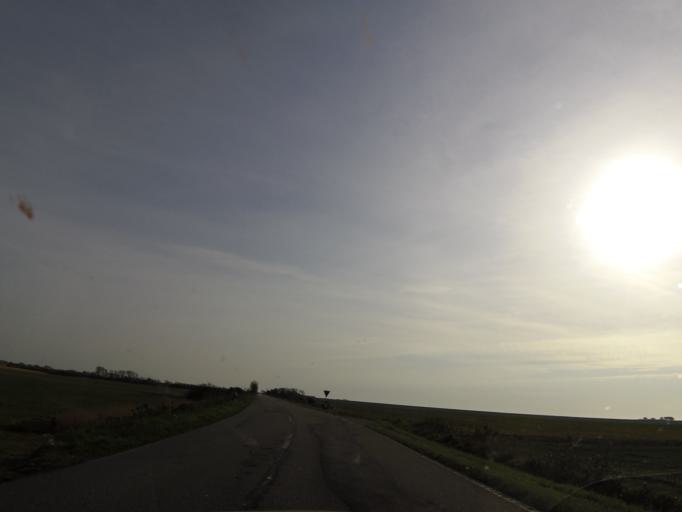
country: DE
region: Schleswig-Holstein
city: Galmsbull
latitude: 54.7502
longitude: 8.7420
